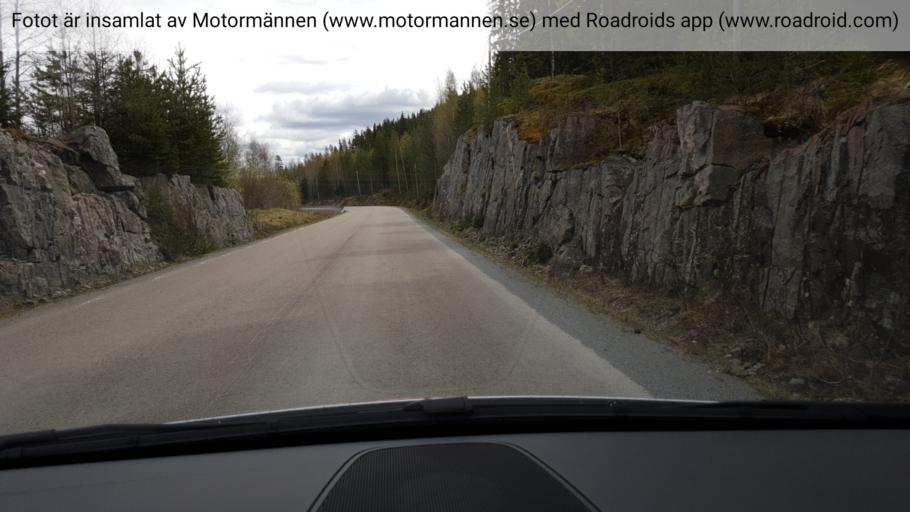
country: SE
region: Jaemtland
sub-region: Bergs Kommun
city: Hoverberg
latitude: 62.6588
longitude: 14.7857
